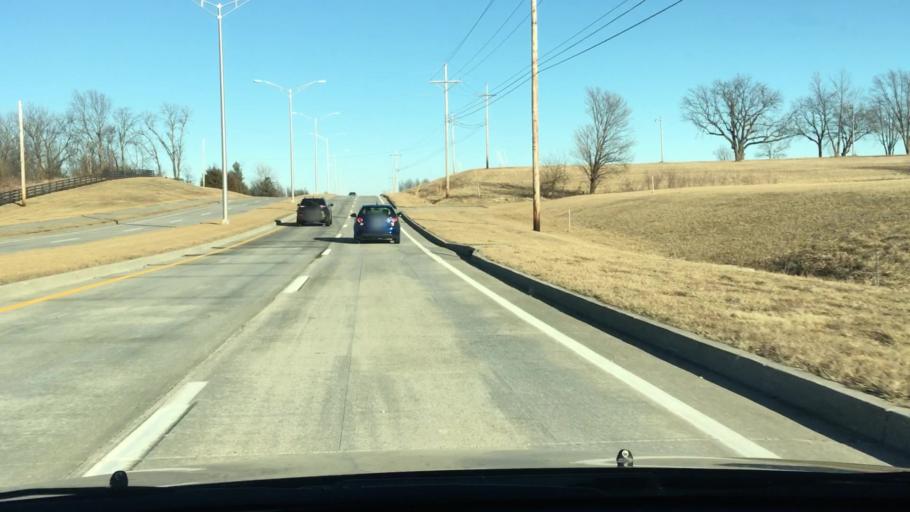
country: US
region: Missouri
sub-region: Cass County
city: Raymore
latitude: 38.8539
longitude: -94.4250
